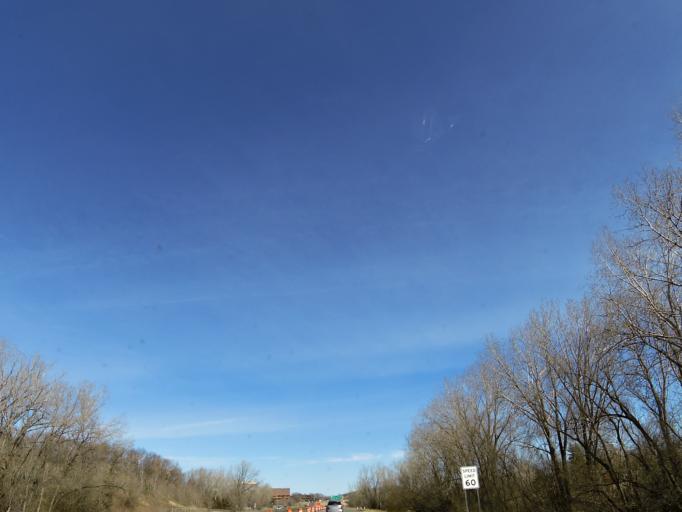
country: US
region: Minnesota
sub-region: Hennepin County
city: Eden Prairie
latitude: 44.8748
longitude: -93.4151
